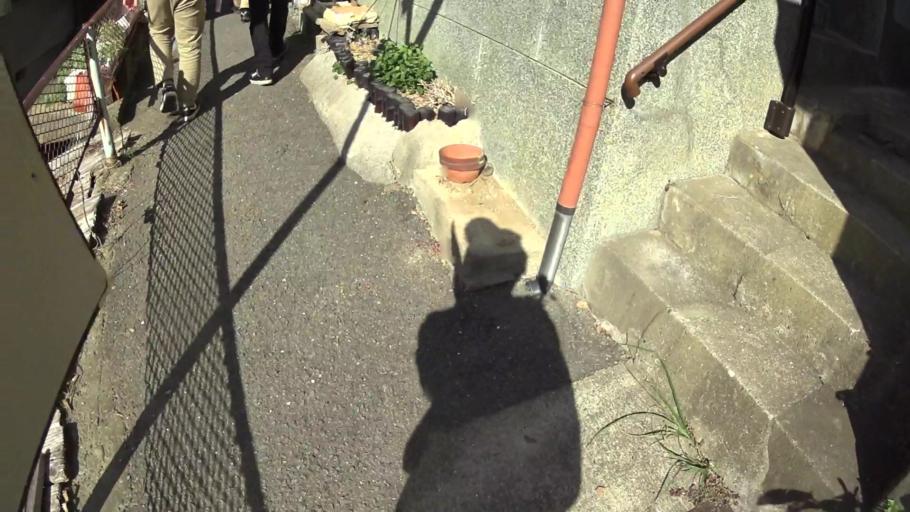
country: JP
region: Wakayama
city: Minato
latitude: 34.1916
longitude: 135.1433
